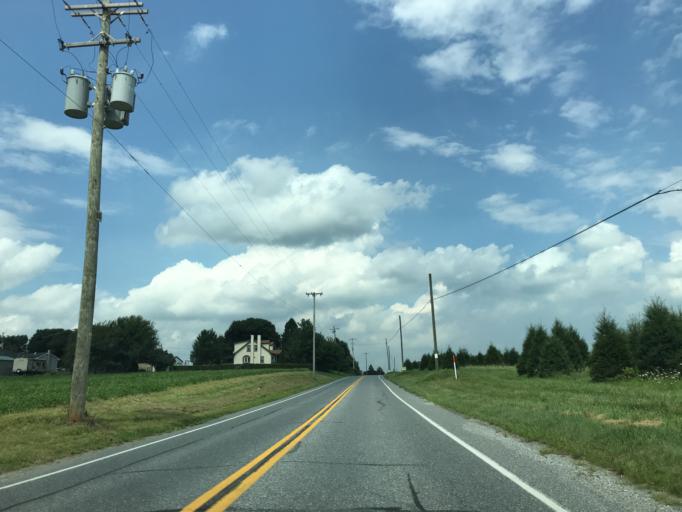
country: US
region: Pennsylvania
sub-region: York County
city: Red Lion
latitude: 39.8574
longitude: -76.6212
